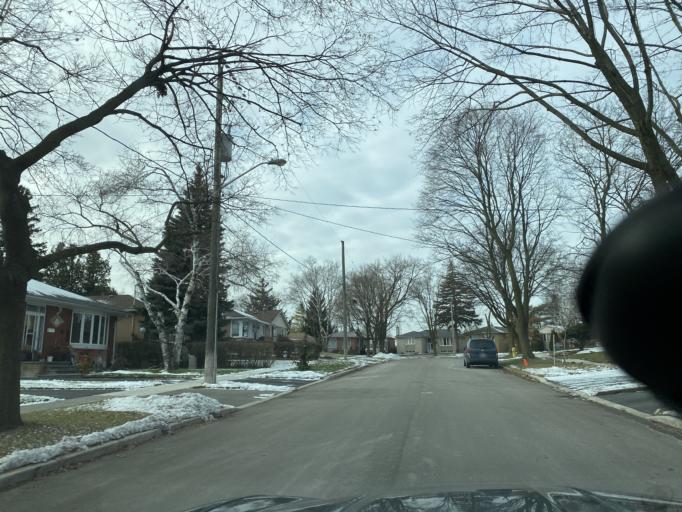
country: CA
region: Ontario
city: Etobicoke
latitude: 43.6646
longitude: -79.5835
